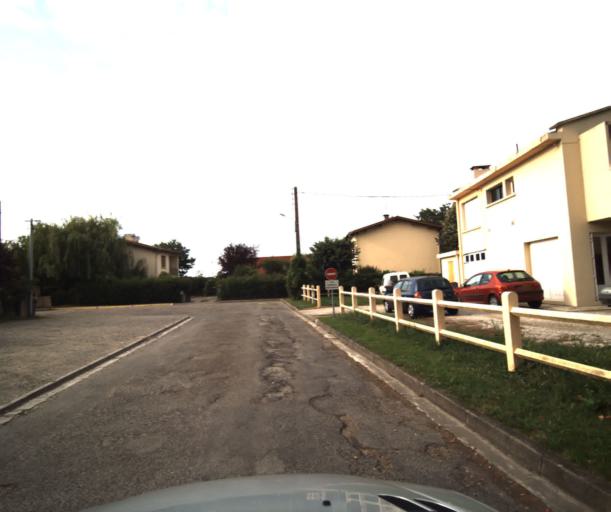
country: FR
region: Midi-Pyrenees
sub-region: Departement de la Haute-Garonne
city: Labarthe-sur-Leze
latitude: 43.4521
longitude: 1.3983
